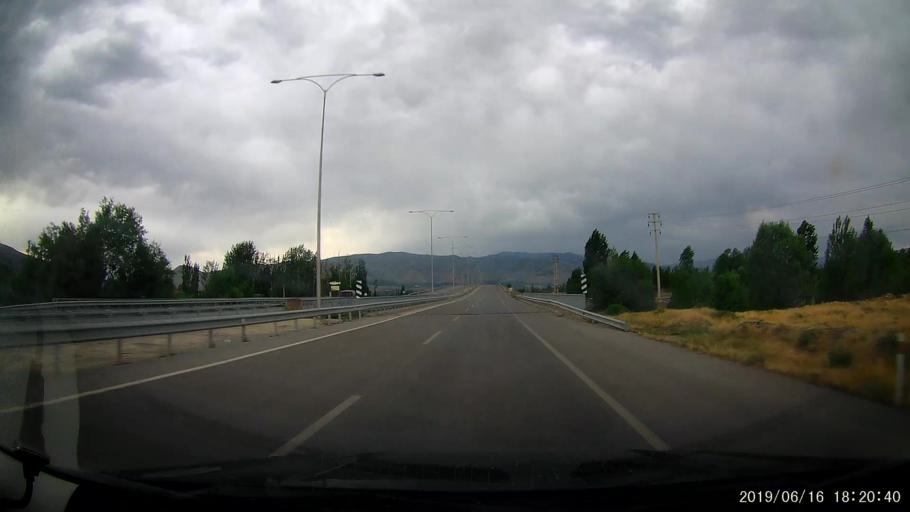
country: TR
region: Erzincan
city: Erzincan
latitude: 39.7203
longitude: 39.4634
